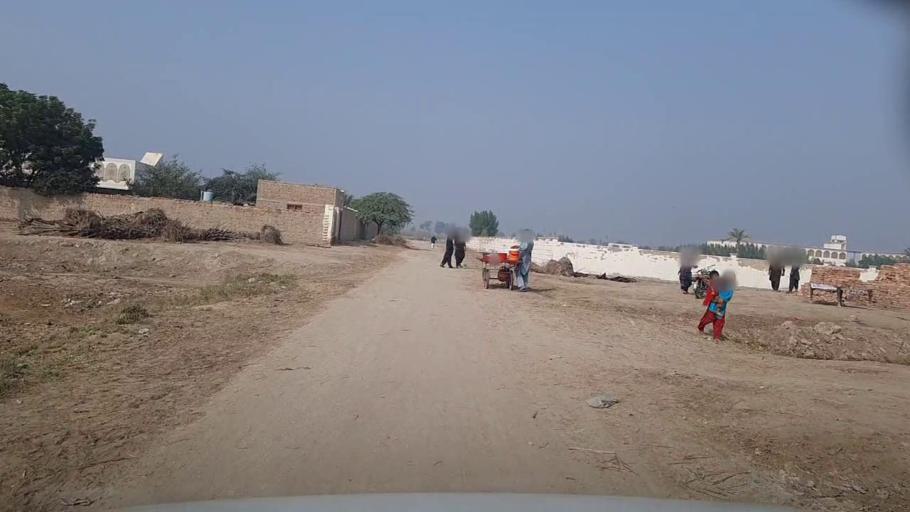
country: PK
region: Sindh
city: Setharja Old
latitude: 27.1917
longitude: 68.4731
